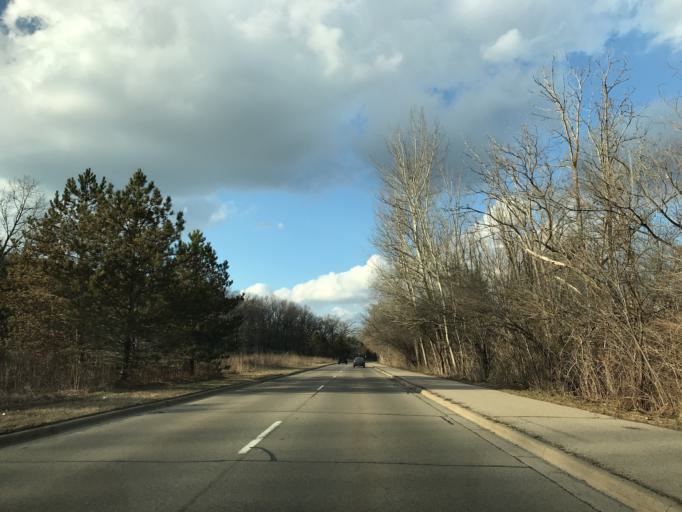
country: US
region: Michigan
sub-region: Washtenaw County
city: Ann Arbor
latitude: 42.2847
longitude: -83.7017
